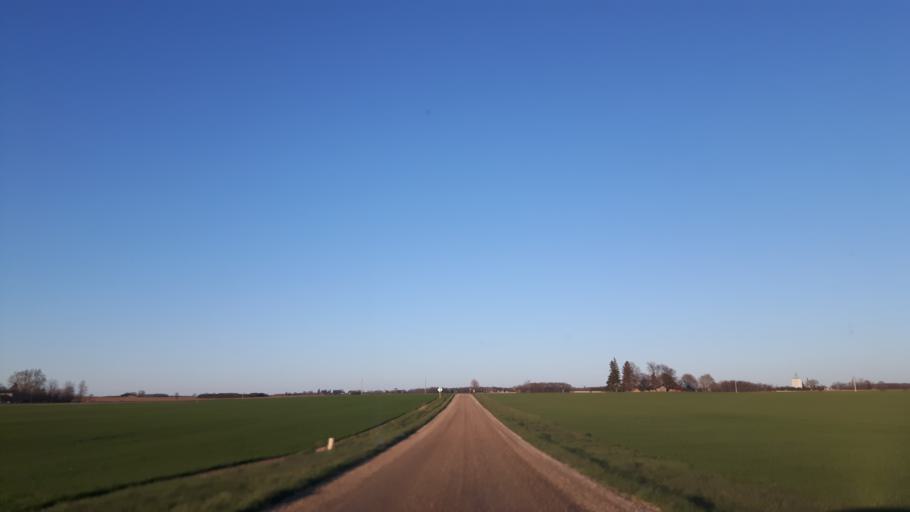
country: CA
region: Ontario
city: Bluewater
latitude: 43.5611
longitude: -81.5313
